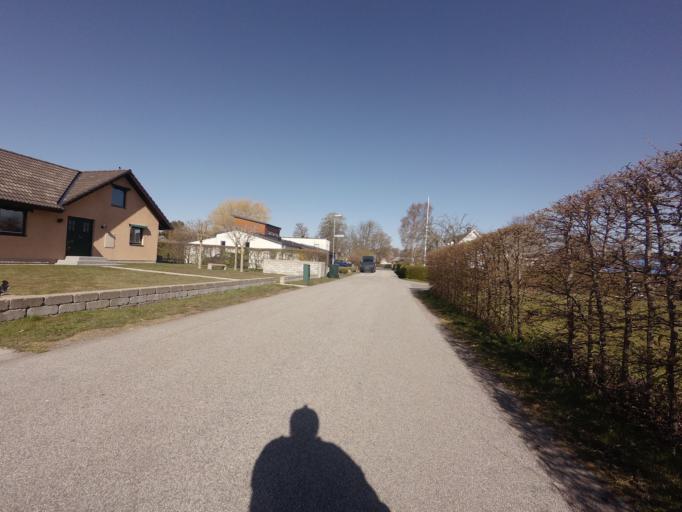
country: SE
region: Skane
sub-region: Lomma Kommun
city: Lomma
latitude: 55.6983
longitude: 13.0525
